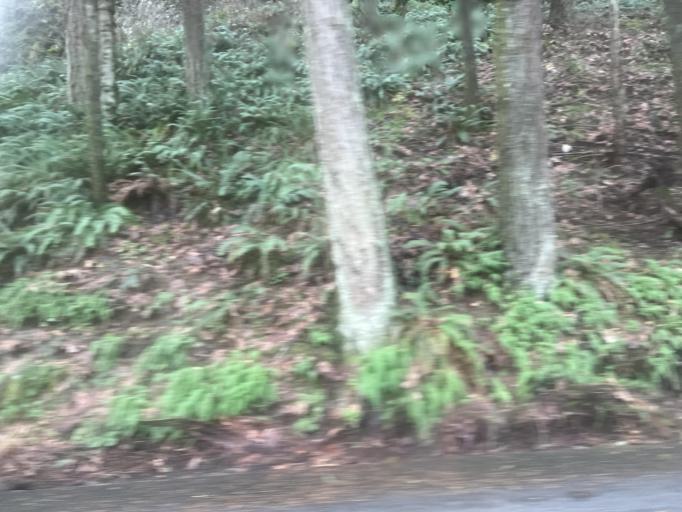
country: US
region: Washington
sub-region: Clark County
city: Washougal
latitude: 45.5416
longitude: -122.2057
